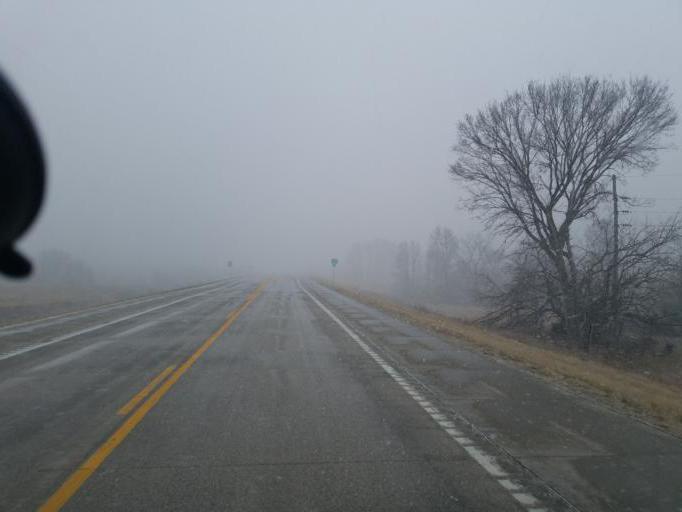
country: US
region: Missouri
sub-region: Adair County
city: Kirksville
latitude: 40.2253
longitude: -92.5639
